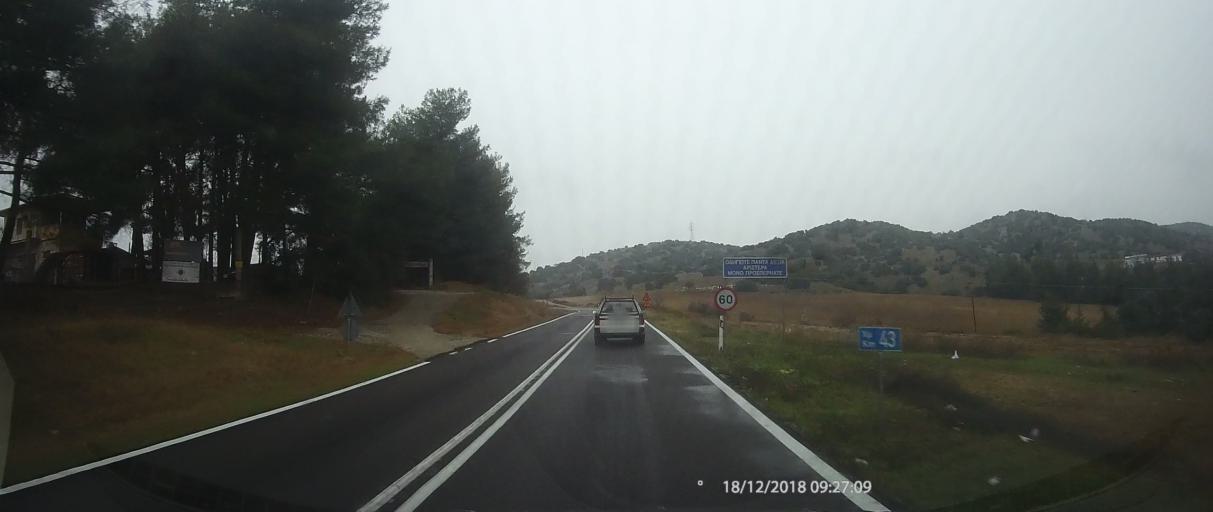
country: GR
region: Thessaly
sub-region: Nomos Larisis
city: Elassona
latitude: 39.9163
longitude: 22.1795
